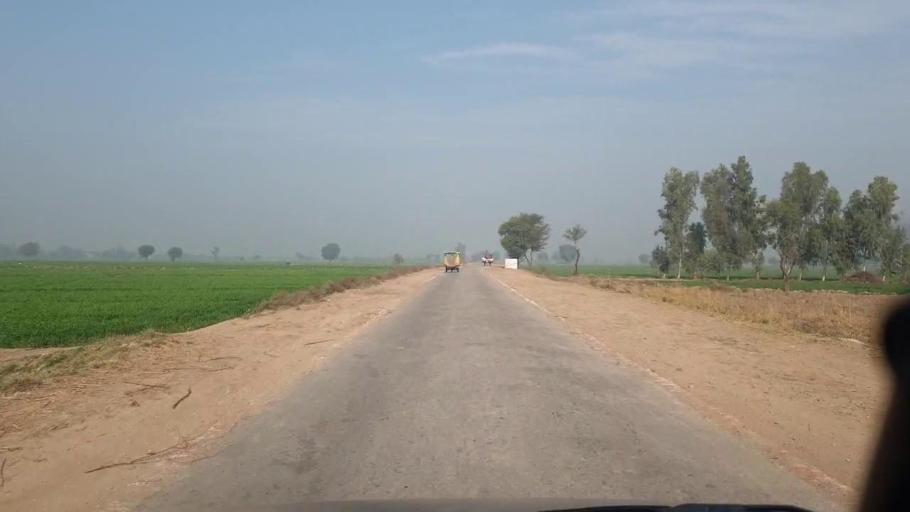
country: PK
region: Sindh
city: Shahdadpur
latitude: 25.9581
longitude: 68.5877
